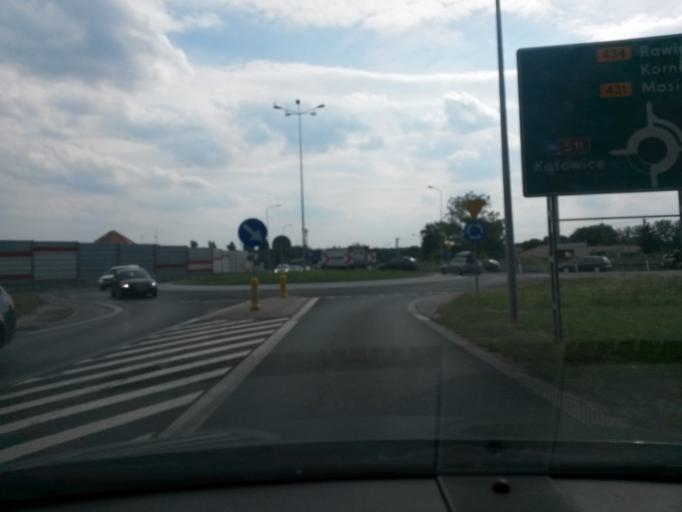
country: PL
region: Greater Poland Voivodeship
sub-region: Powiat poznanski
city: Kornik
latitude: 52.2575
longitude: 17.0797
